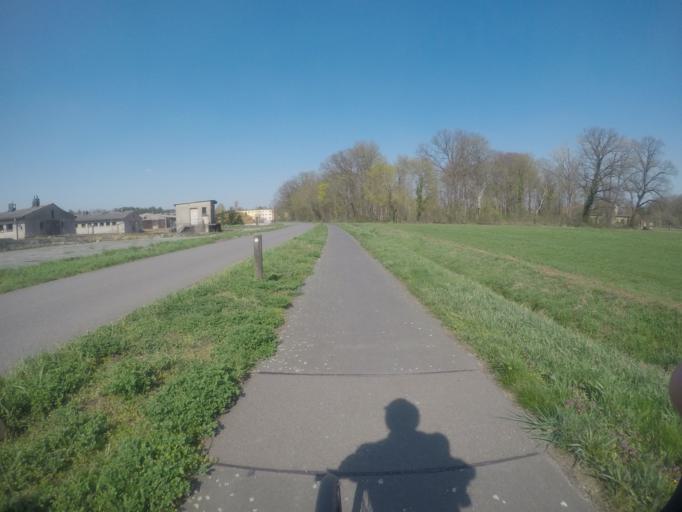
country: DE
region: Brandenburg
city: Falkensee
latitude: 52.6360
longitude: 13.0856
